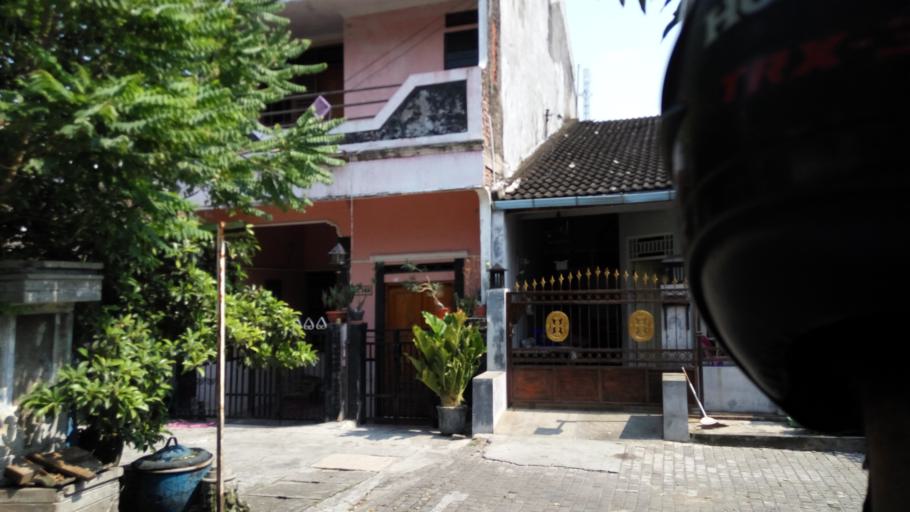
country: ID
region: Central Java
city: Mranggen
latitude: -7.0316
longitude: 110.4730
